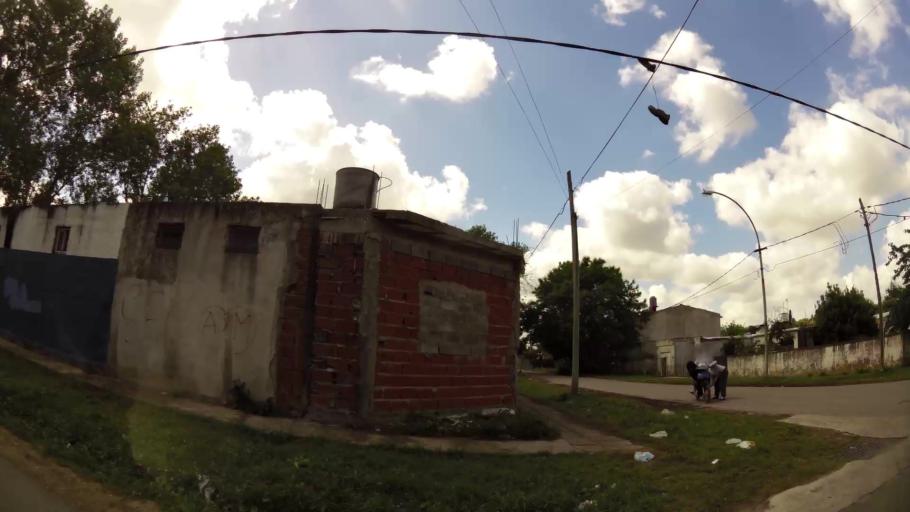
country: AR
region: Buenos Aires
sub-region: Partido de Quilmes
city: Quilmes
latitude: -34.8290
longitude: -58.1894
